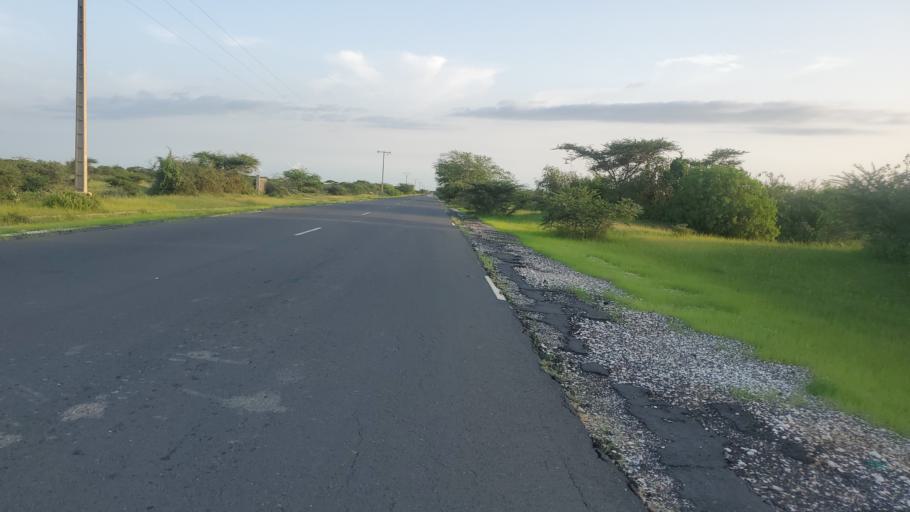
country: SN
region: Saint-Louis
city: Saint-Louis
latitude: 16.1801
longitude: -16.4095
